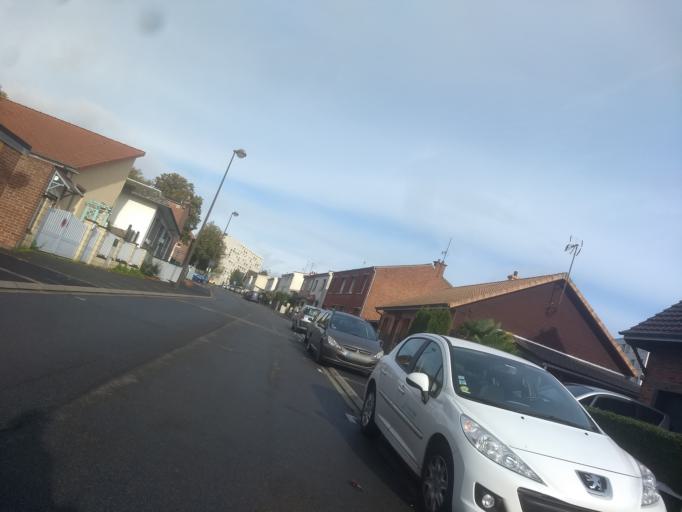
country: FR
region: Nord-Pas-de-Calais
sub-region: Departement du Pas-de-Calais
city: Achicourt
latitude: 50.2884
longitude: 2.7522
